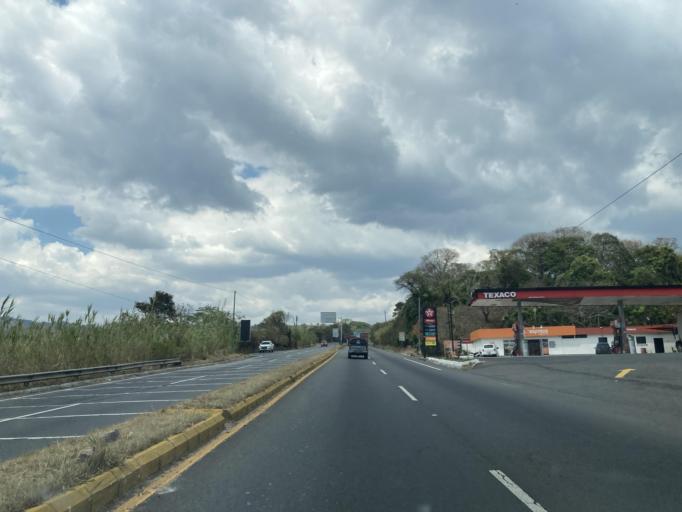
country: GT
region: Guatemala
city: Fraijanes
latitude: 14.4181
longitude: -90.4789
